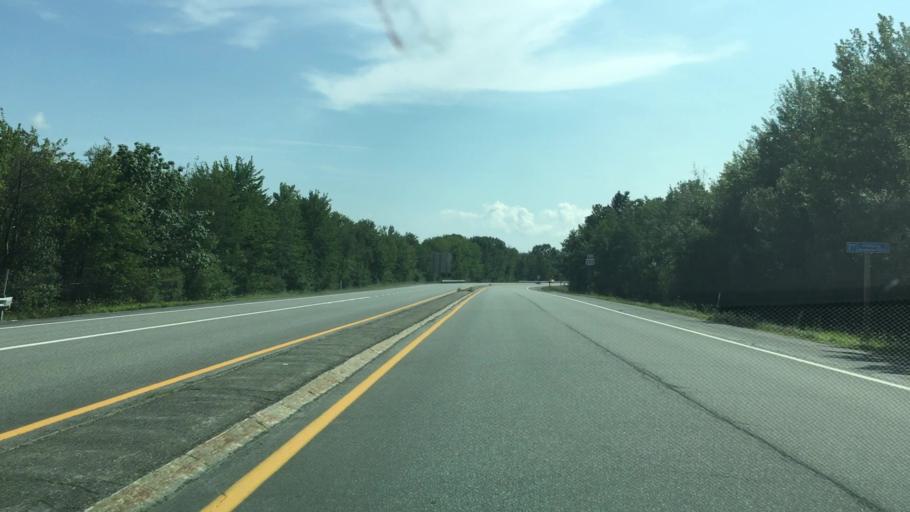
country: US
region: Maine
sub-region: Penobscot County
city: Bangor
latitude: 44.7833
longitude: -68.7950
